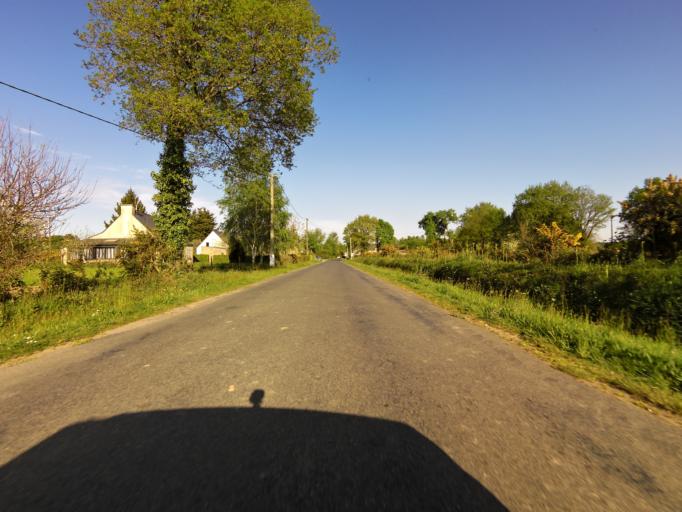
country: FR
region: Brittany
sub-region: Departement du Morbihan
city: Molac
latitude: 47.7429
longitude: -2.4638
